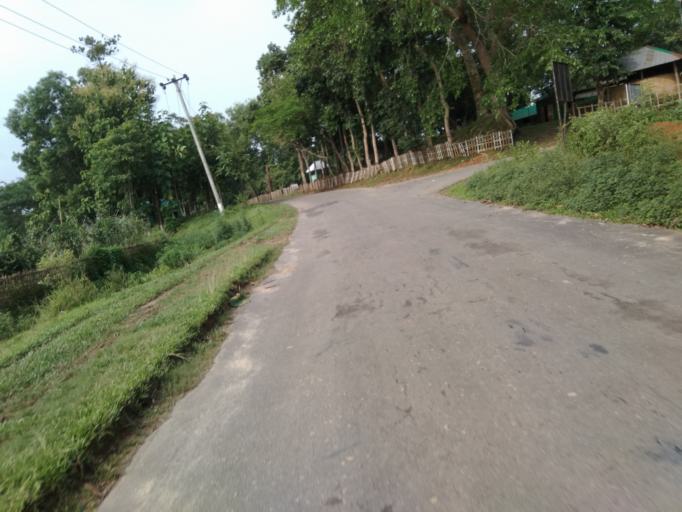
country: BD
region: Chittagong
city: Khagrachhari
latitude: 23.0202
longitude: 92.0140
